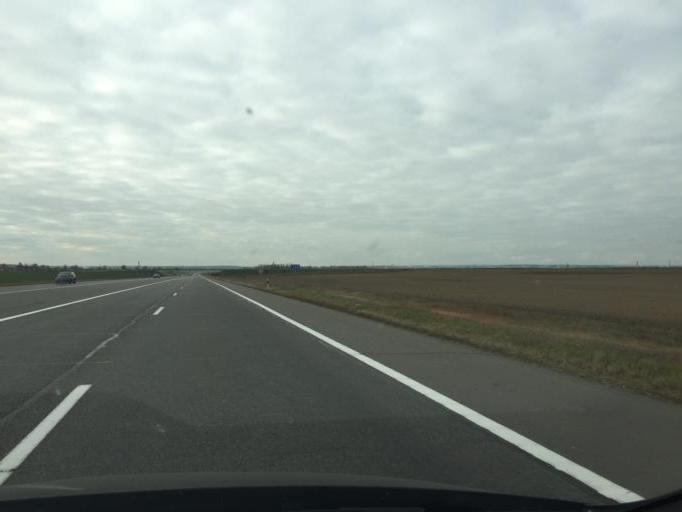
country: BY
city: Fanipol
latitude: 53.6816
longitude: 27.2906
